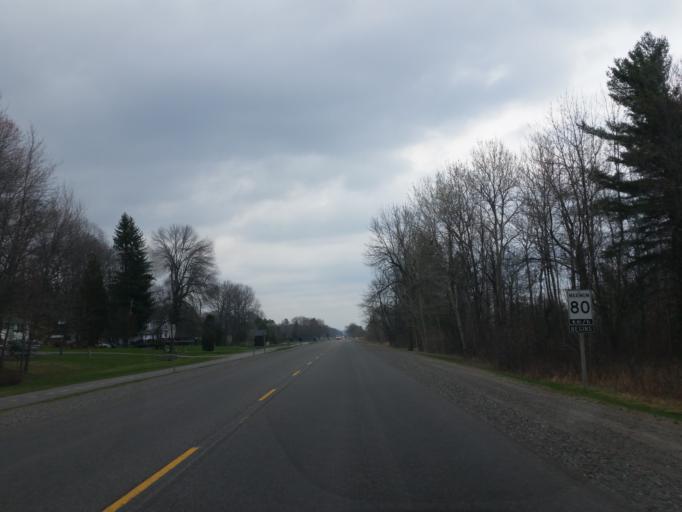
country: US
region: New York
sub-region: Jefferson County
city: Alexandria Bay
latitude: 44.4572
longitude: -75.8561
